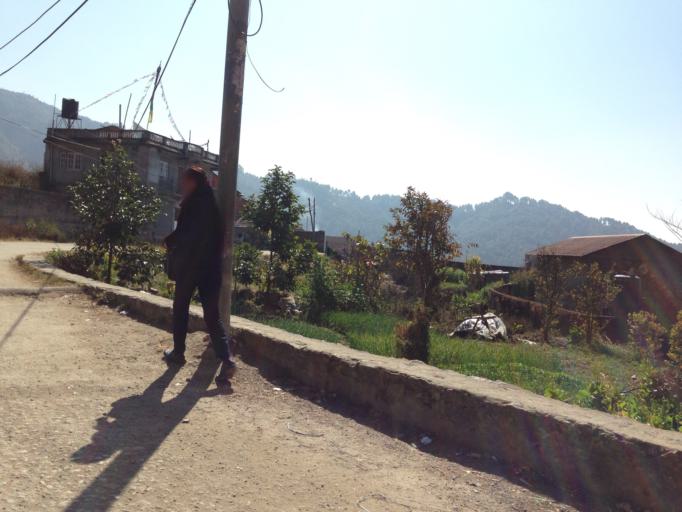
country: NP
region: Central Region
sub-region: Bagmati Zone
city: Kathmandu
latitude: 27.7785
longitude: 85.3674
